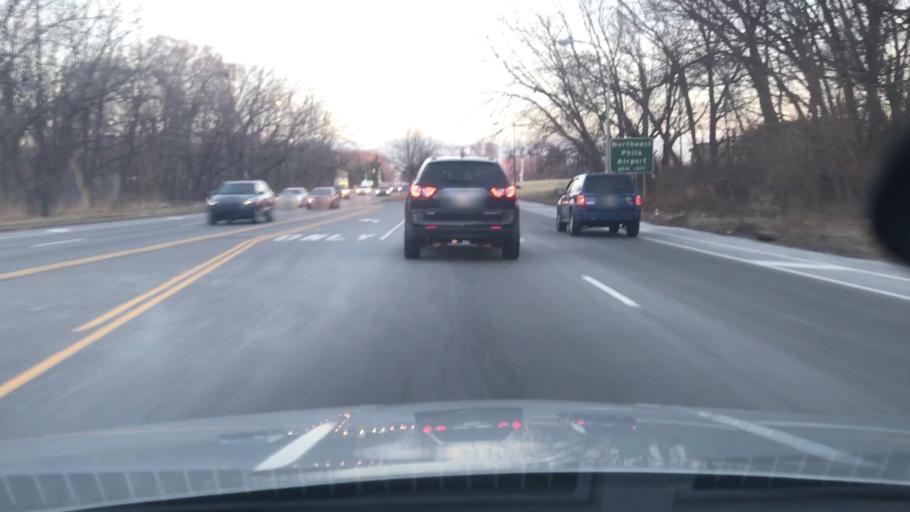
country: US
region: New Jersey
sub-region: Burlington County
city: Riverton
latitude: 40.0735
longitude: -75.0157
